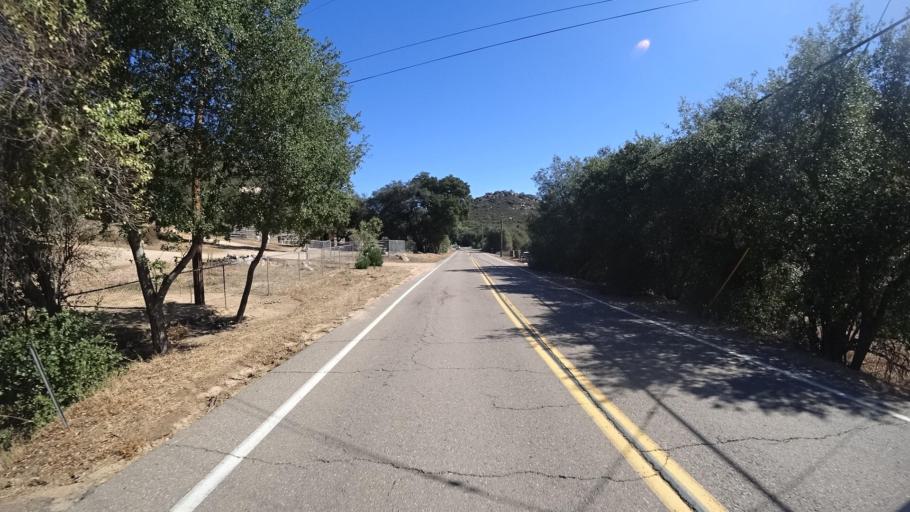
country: US
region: California
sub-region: San Diego County
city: Descanso
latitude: 32.8120
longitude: -116.6343
